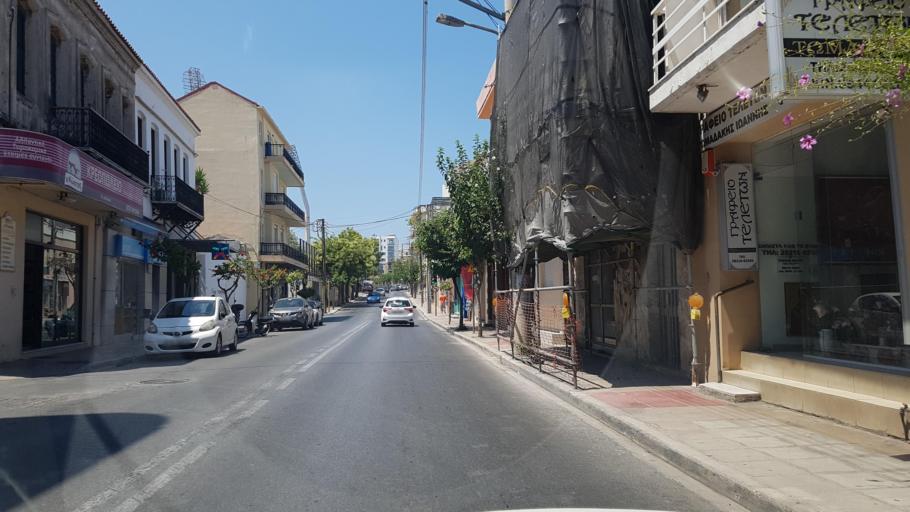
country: GR
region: Crete
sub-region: Nomos Chanias
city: Chania
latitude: 35.5145
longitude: 24.0273
